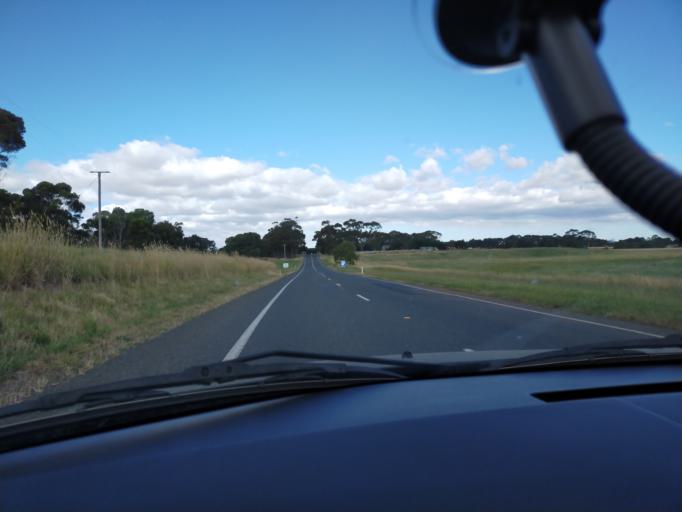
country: AU
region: Victoria
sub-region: Colac-Otway
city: Colac
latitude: -38.0240
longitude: 143.6236
